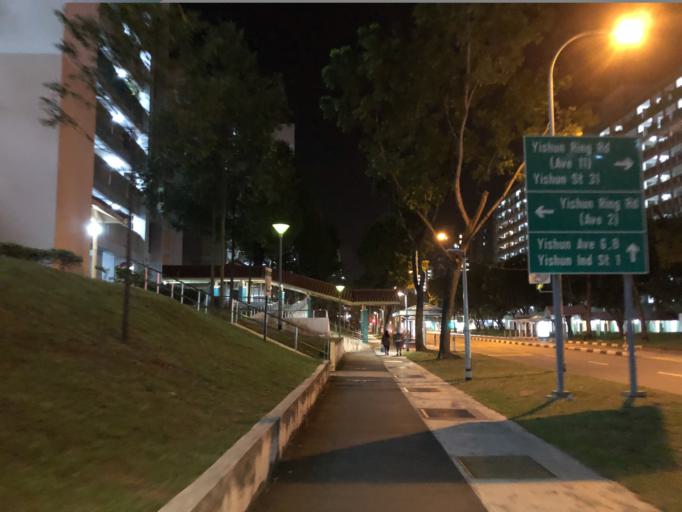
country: MY
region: Johor
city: Kampung Pasir Gudang Baru
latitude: 1.4319
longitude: 103.8396
